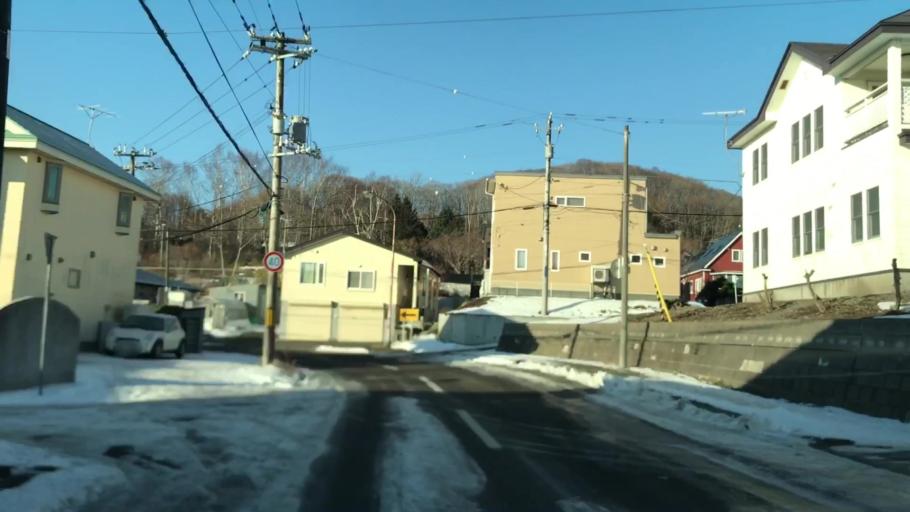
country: JP
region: Hokkaido
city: Muroran
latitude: 42.3891
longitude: 141.0660
